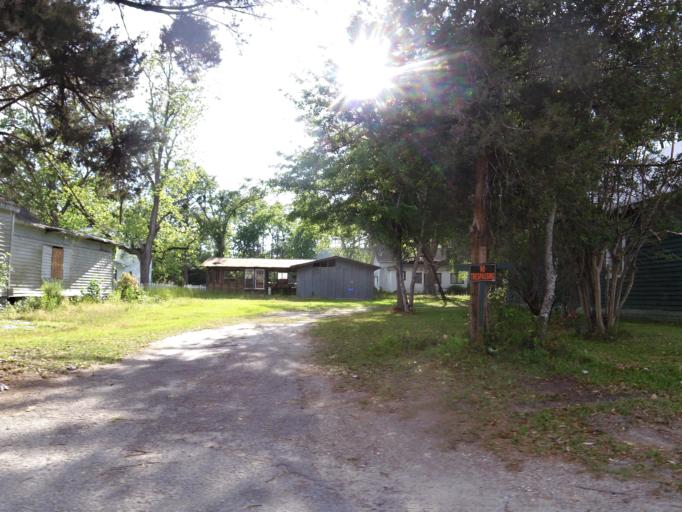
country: US
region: South Carolina
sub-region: Hampton County
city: Estill
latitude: 32.7575
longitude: -81.2419
